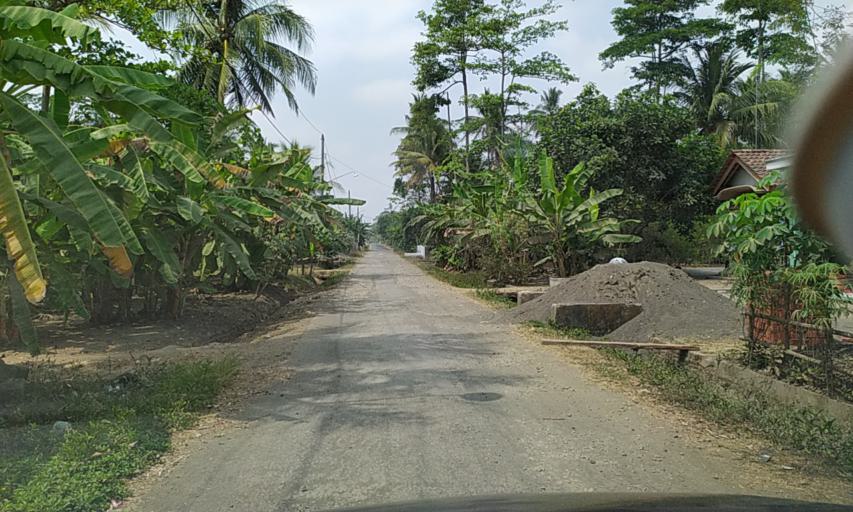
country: ID
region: Central Java
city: Wanadadi
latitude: -7.5272
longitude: 108.8327
